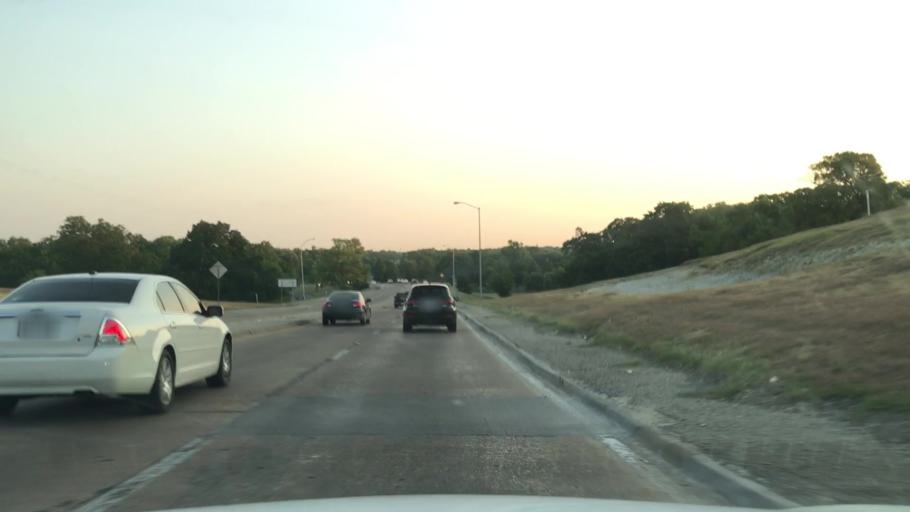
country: US
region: Texas
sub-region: Dallas County
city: Highland Park
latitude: 32.8544
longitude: -96.7177
